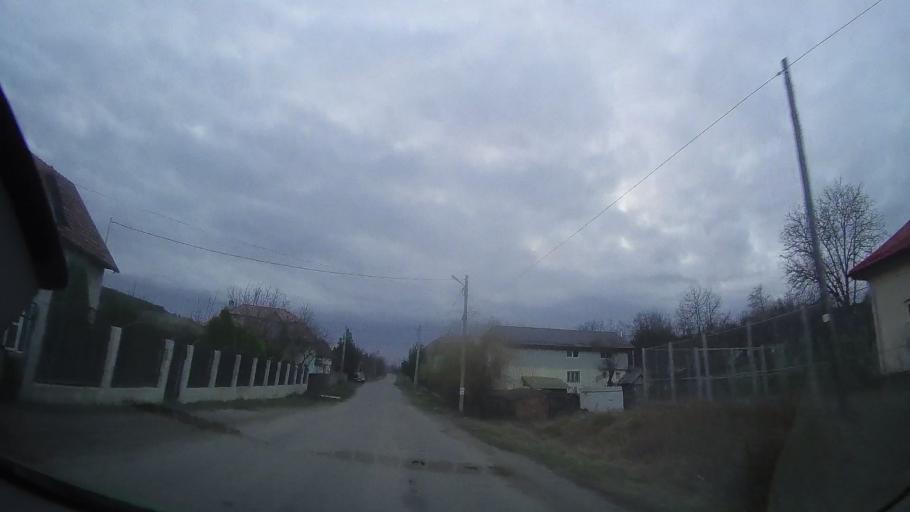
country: RO
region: Cluj
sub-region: Comuna Caianu
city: Vaida-Camaras
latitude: 46.8321
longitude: 23.9559
